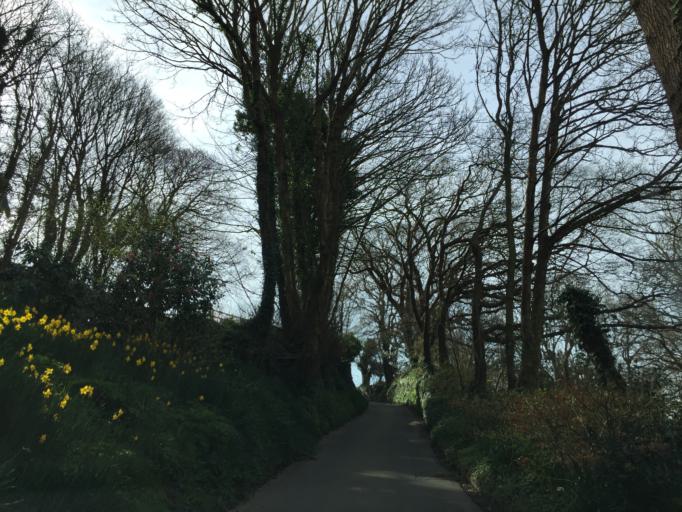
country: JE
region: St Helier
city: Saint Helier
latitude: 49.2194
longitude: -2.1455
